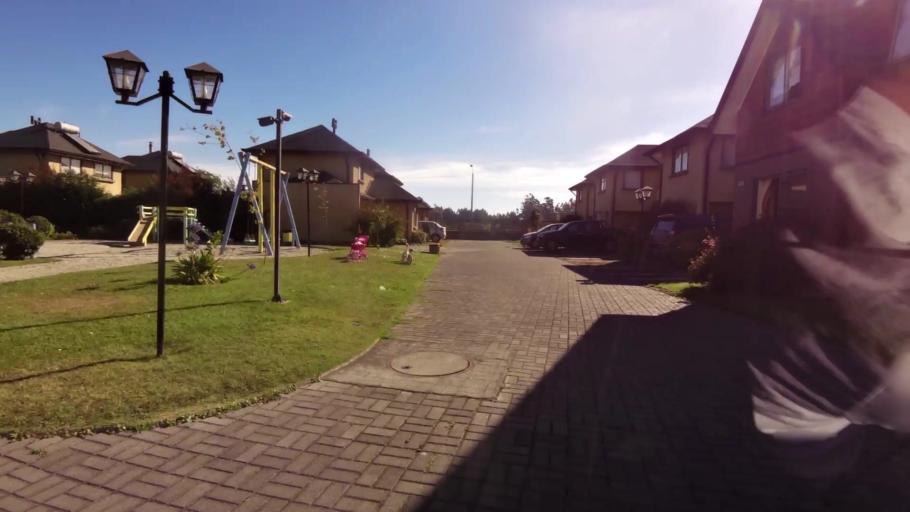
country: CL
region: Biobio
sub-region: Provincia de Concepcion
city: Concepcion
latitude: -36.8442
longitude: -73.1207
